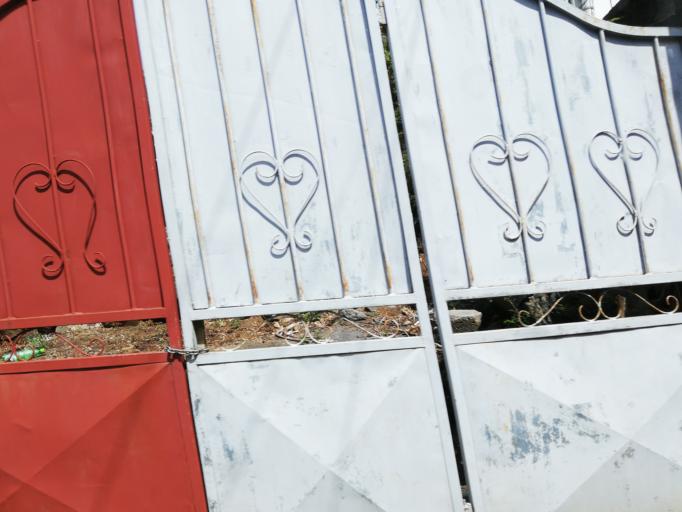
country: MU
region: Moka
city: Moka
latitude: -20.2177
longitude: 57.4703
